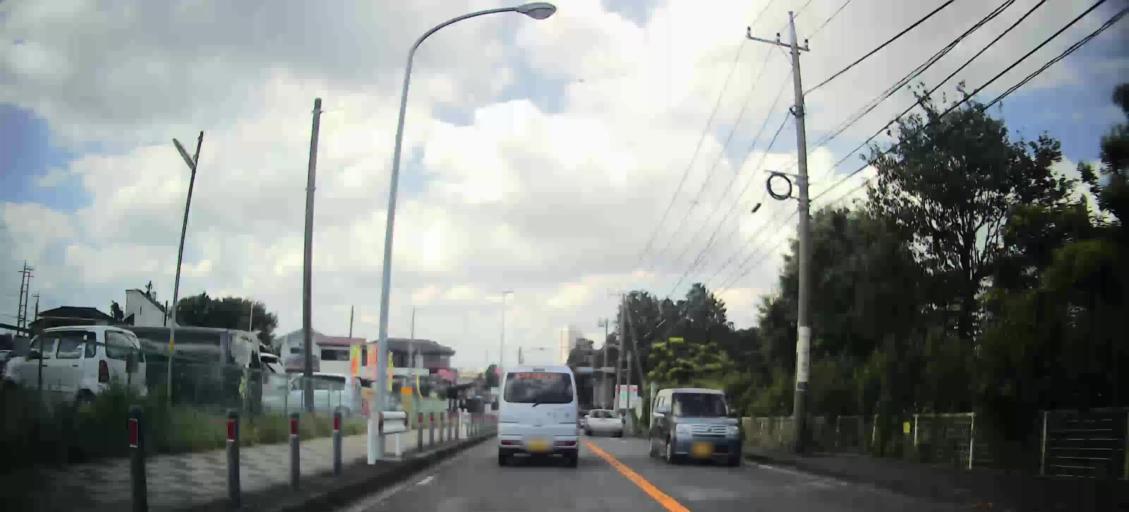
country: JP
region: Kanagawa
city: Yokohama
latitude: 35.4689
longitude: 139.5584
